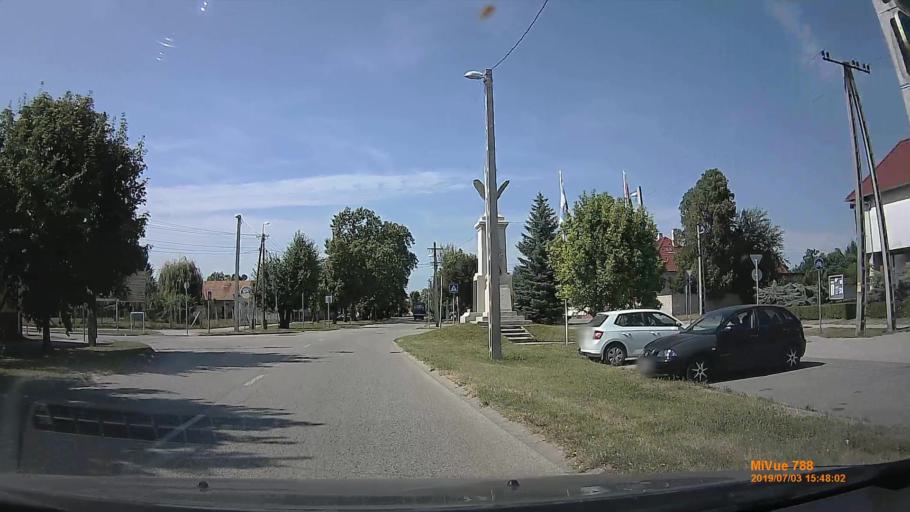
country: HU
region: Gyor-Moson-Sopron
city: Toltestava
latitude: 47.6945
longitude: 17.7408
